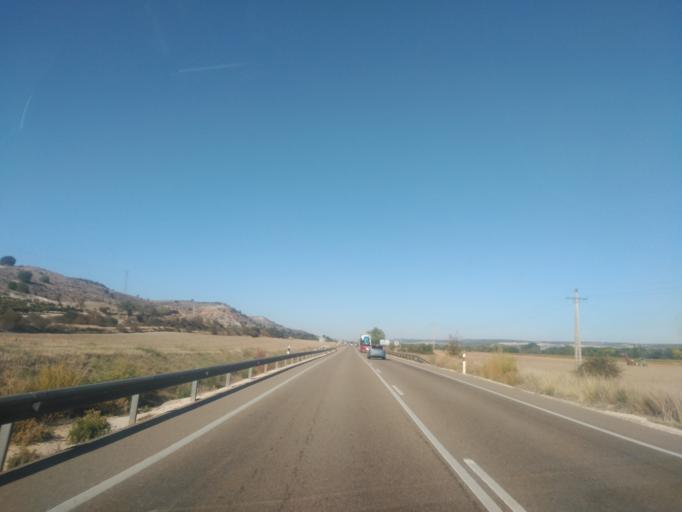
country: ES
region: Castille and Leon
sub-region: Provincia de Valladolid
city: Quintanilla de Arriba
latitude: 41.6206
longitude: -4.2335
